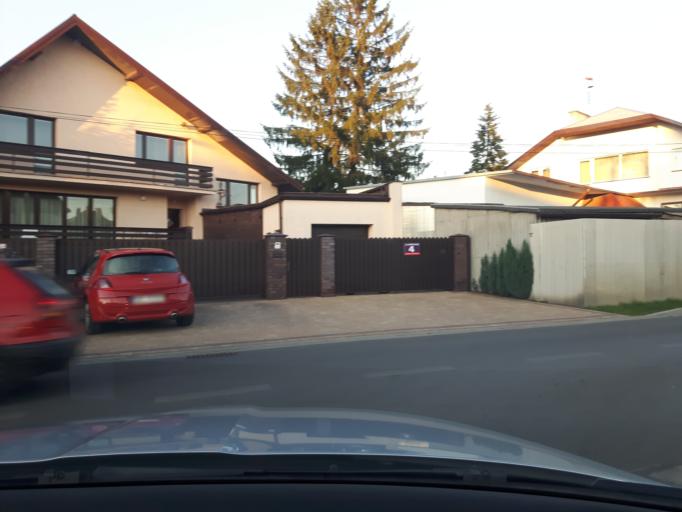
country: PL
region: Masovian Voivodeship
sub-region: Powiat wolominski
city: Kobylka
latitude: 52.3315
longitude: 21.1921
